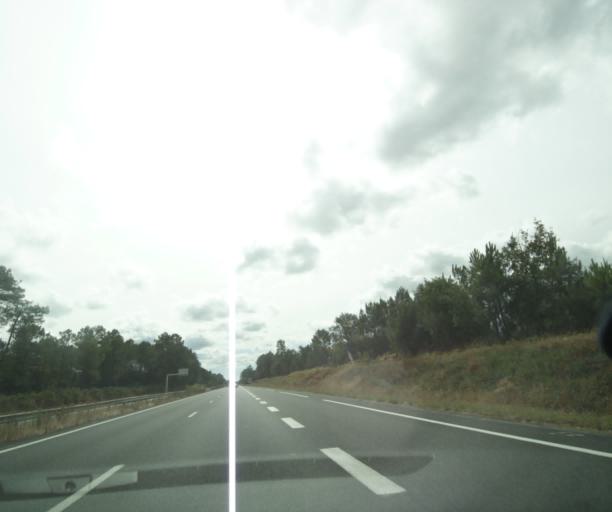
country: FR
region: Aquitaine
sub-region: Departement de la Gironde
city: Marcillac
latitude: 45.2519
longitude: -0.5405
